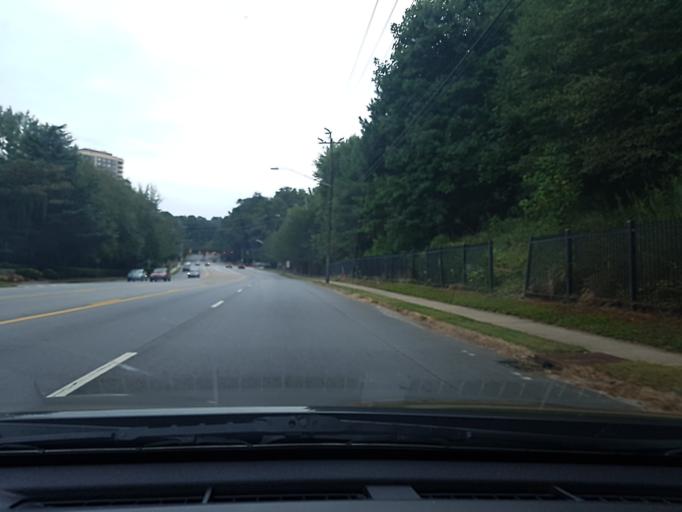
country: US
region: Georgia
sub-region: DeKalb County
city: North Decatur
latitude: 33.8002
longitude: -84.3088
